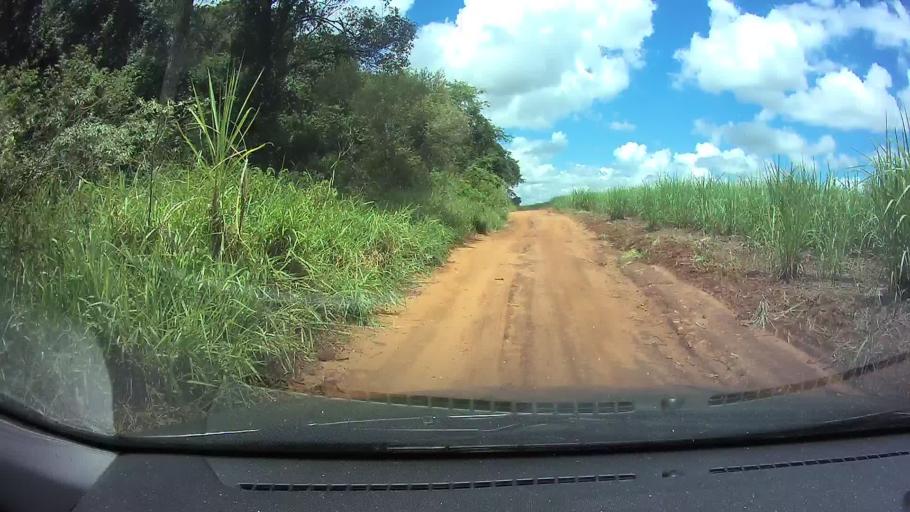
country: PY
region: Paraguari
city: La Colmena
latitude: -25.9513
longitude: -56.7753
